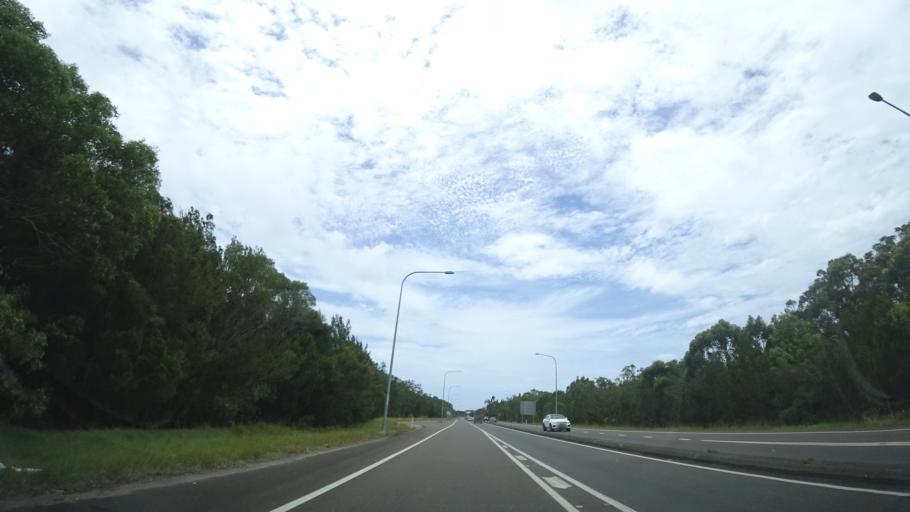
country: AU
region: Queensland
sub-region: Sunshine Coast
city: Mooloolaba
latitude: -26.7120
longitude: 153.0913
